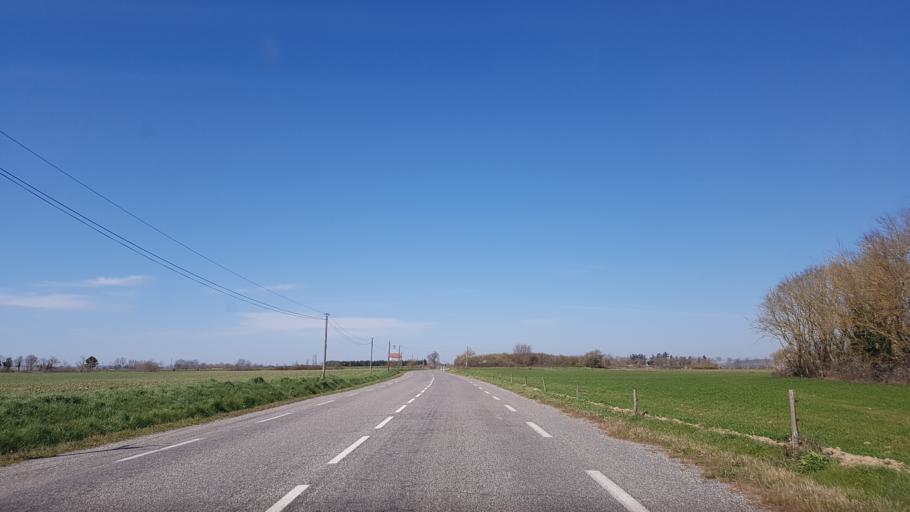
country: FR
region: Midi-Pyrenees
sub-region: Departement de l'Ariege
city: Mazeres
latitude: 43.2307
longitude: 1.6661
